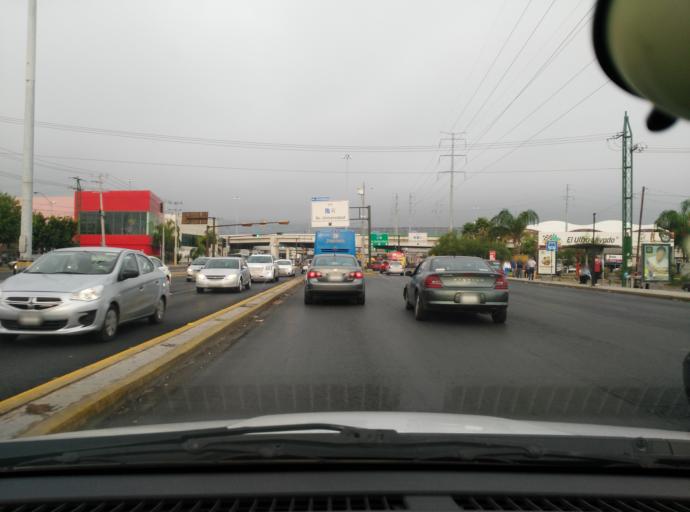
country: MX
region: Nuevo Leon
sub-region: San Nicolas de los Garza
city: San Nicolas de los Garza
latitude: 25.7679
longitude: -100.2902
